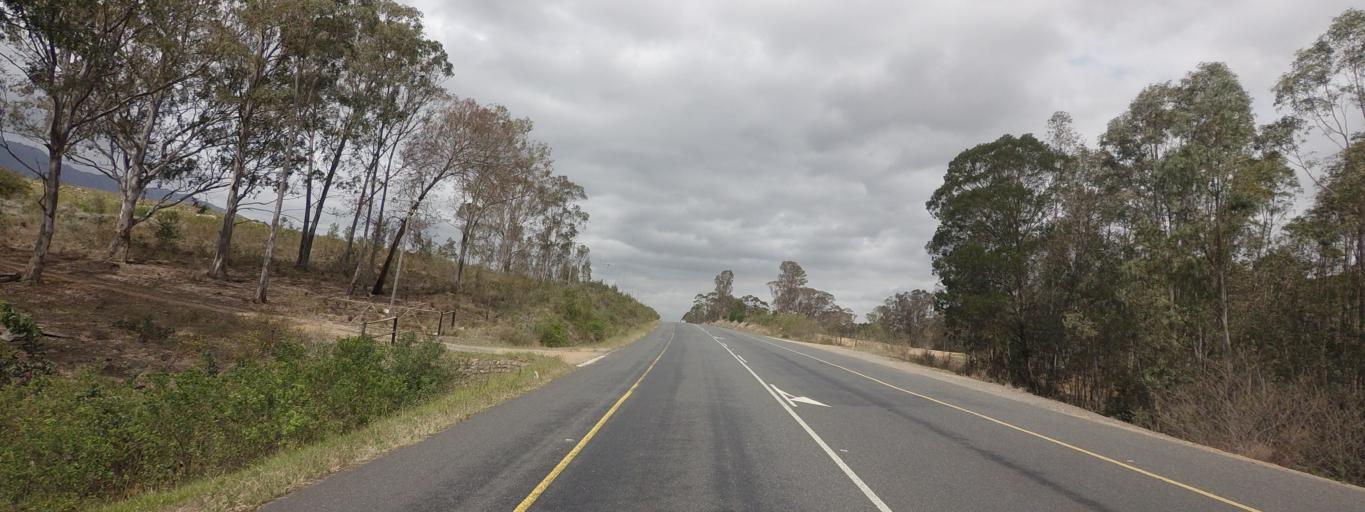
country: ZA
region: Western Cape
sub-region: Overberg District Municipality
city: Swellendam
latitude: -34.0148
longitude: 20.3974
